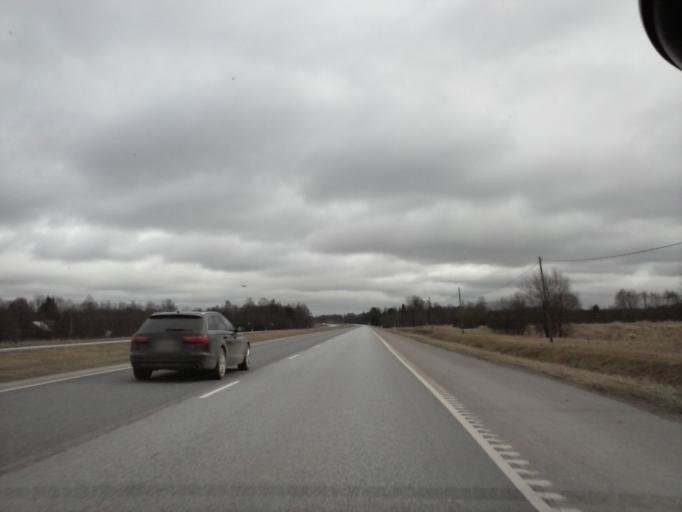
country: EE
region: Harju
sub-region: Rae vald
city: Vaida
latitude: 59.3084
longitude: 24.9396
